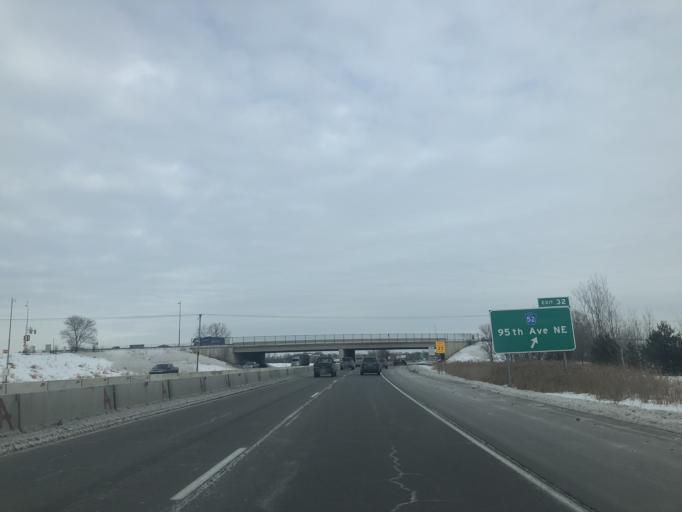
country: US
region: Minnesota
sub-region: Anoka County
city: Lexington
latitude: 45.1409
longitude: -93.1866
